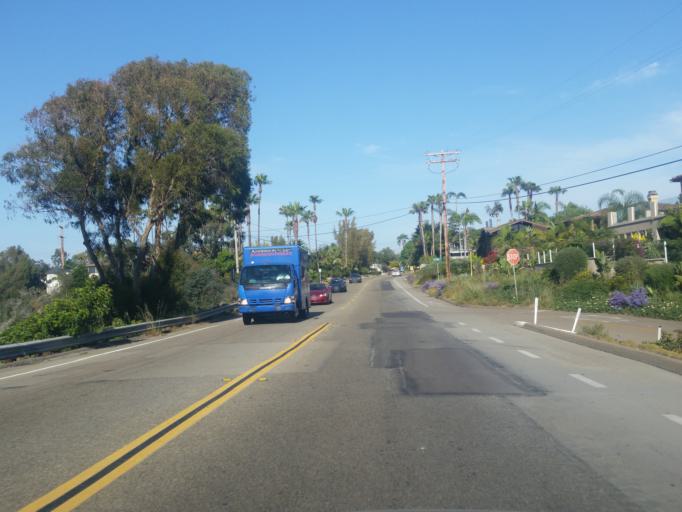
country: US
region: California
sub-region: San Diego County
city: Encinitas
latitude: 33.0835
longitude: -117.3065
